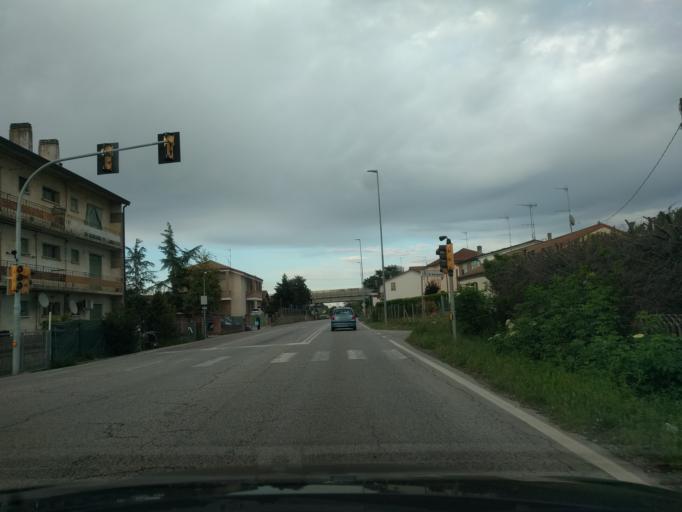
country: IT
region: Veneto
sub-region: Provincia di Rovigo
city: Santa Maria Maddalena
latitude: 44.8914
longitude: 11.6131
